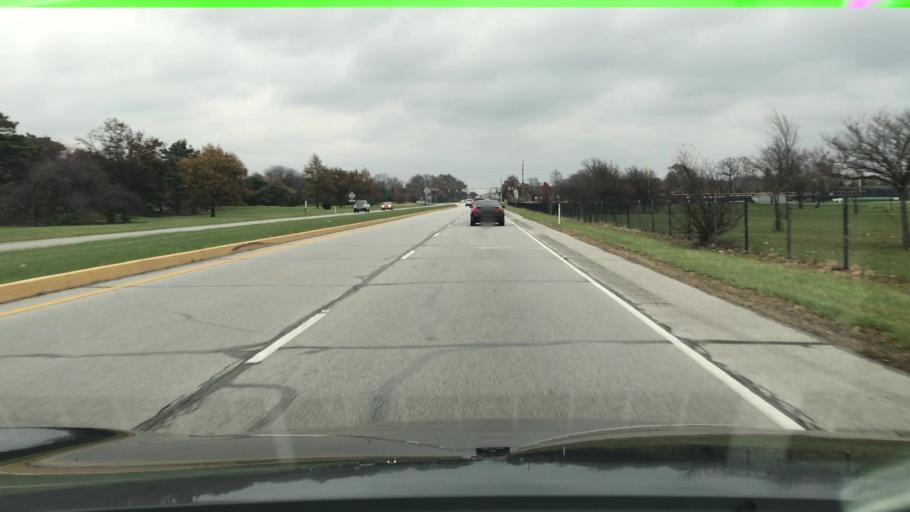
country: US
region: Indiana
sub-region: Delaware County
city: Muncie
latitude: 40.2189
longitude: -85.4245
